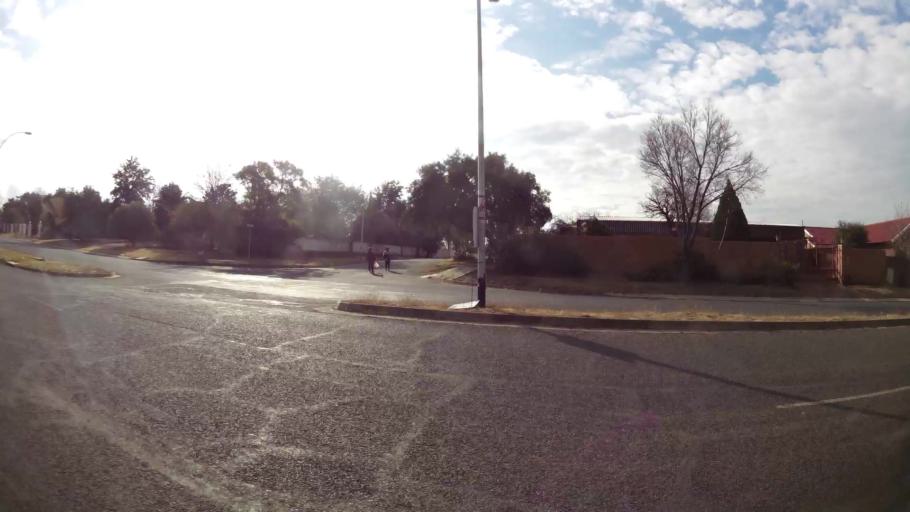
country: ZA
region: Orange Free State
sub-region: Mangaung Metropolitan Municipality
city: Bloemfontein
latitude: -29.0753
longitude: 26.2312
